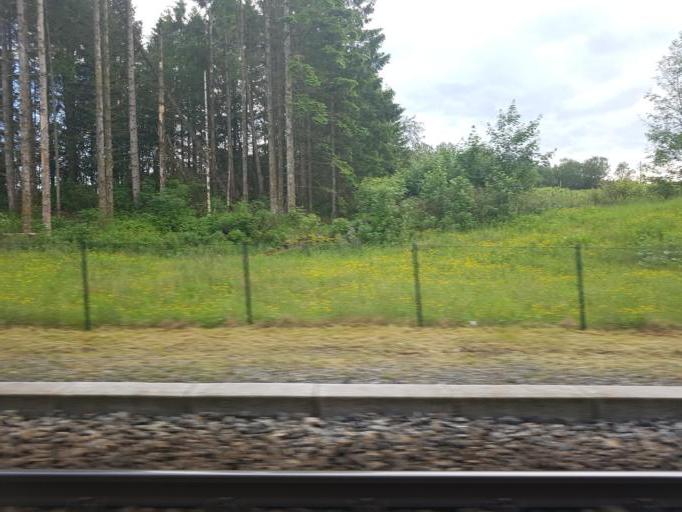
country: NO
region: Hordaland
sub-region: Bergen
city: Ytrebygda
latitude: 60.2881
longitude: 5.2578
